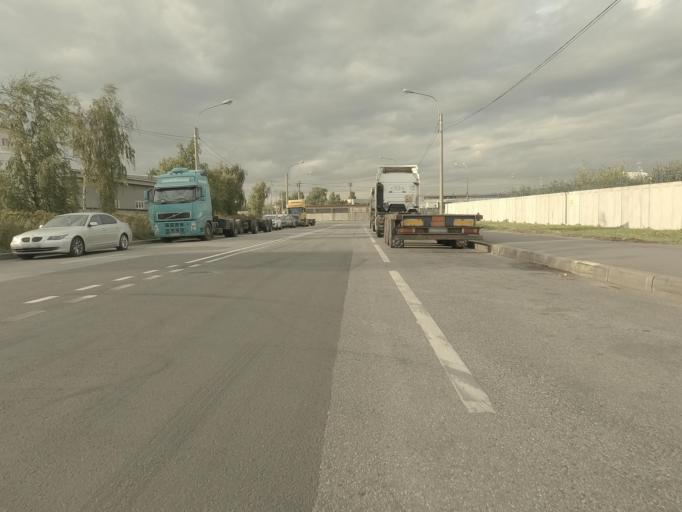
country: RU
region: St.-Petersburg
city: Avtovo
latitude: 59.8672
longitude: 30.2378
